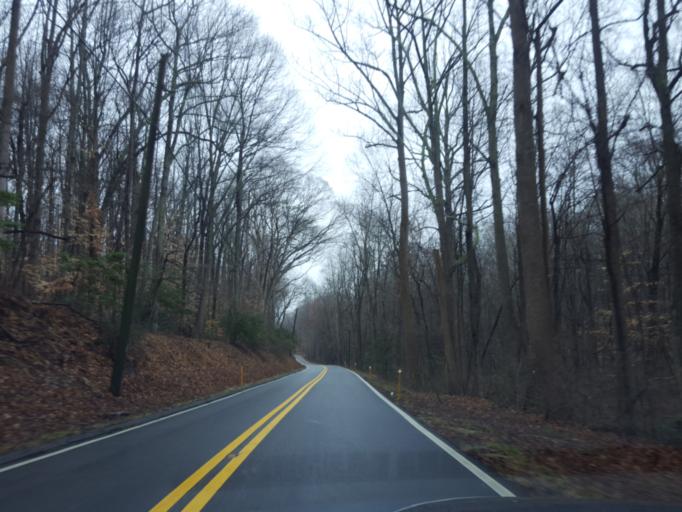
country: US
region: Maryland
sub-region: Calvert County
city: Chesapeake Beach
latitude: 38.6098
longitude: -76.5312
